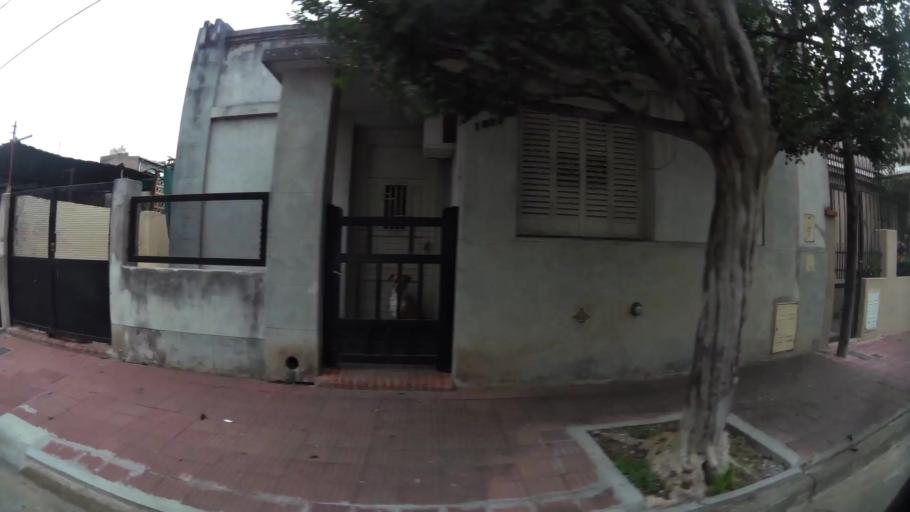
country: AR
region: Santa Fe
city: Granadero Baigorria
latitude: -32.9066
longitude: -60.6936
